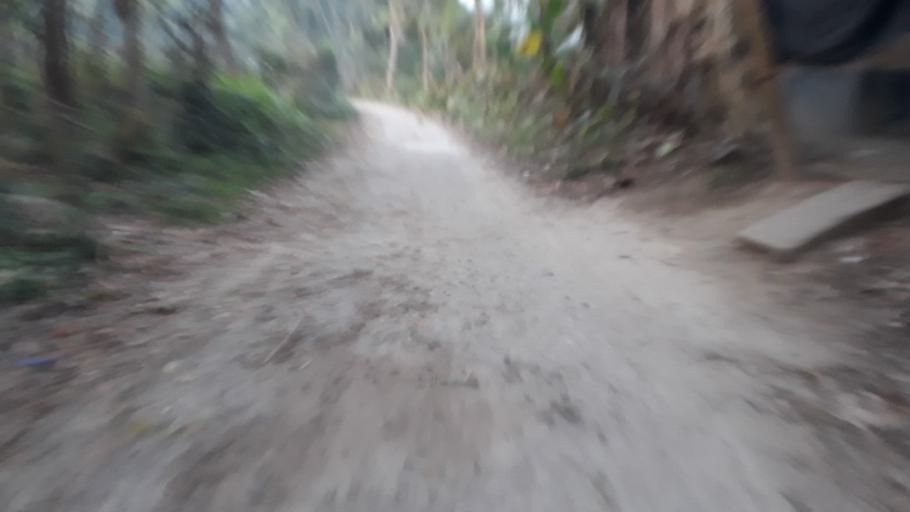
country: BD
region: Khulna
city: Kaliganj
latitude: 23.3494
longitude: 88.9074
